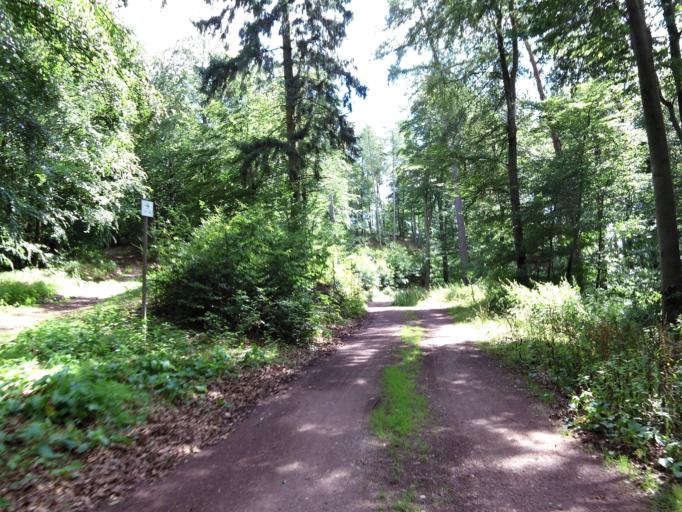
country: DE
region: Thuringia
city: Wolfsburg-Unkeroda
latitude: 50.9472
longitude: 10.2851
